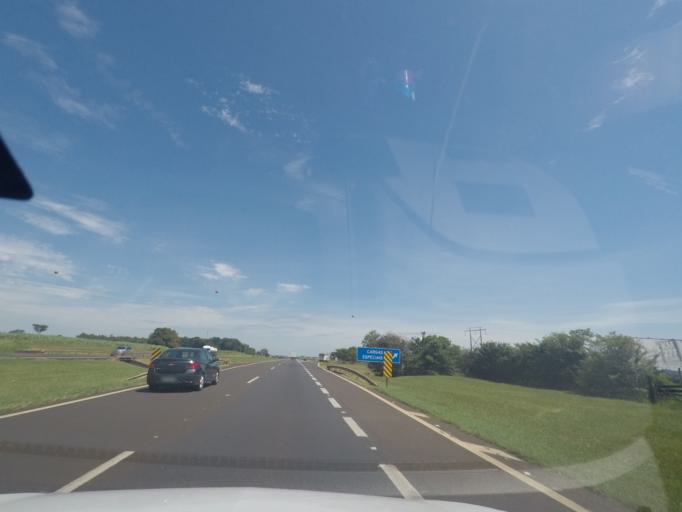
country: BR
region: Sao Paulo
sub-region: Araraquara
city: Araraquara
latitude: -21.8258
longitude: -48.1681
